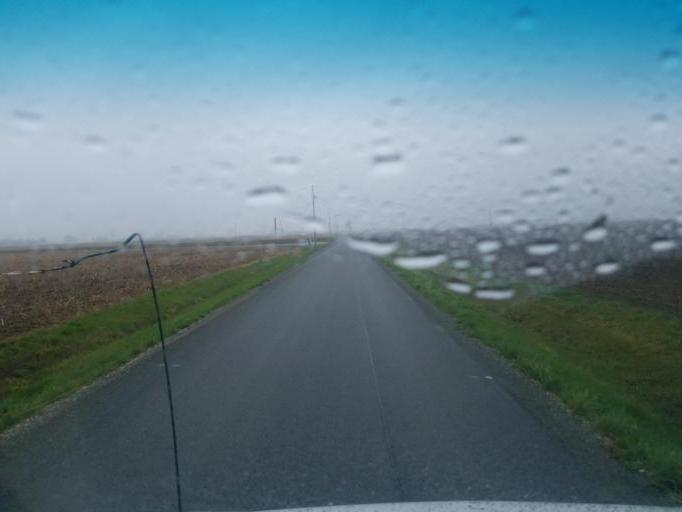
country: US
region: Ohio
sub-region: Wyandot County
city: Carey
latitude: 40.9924
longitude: -83.3408
